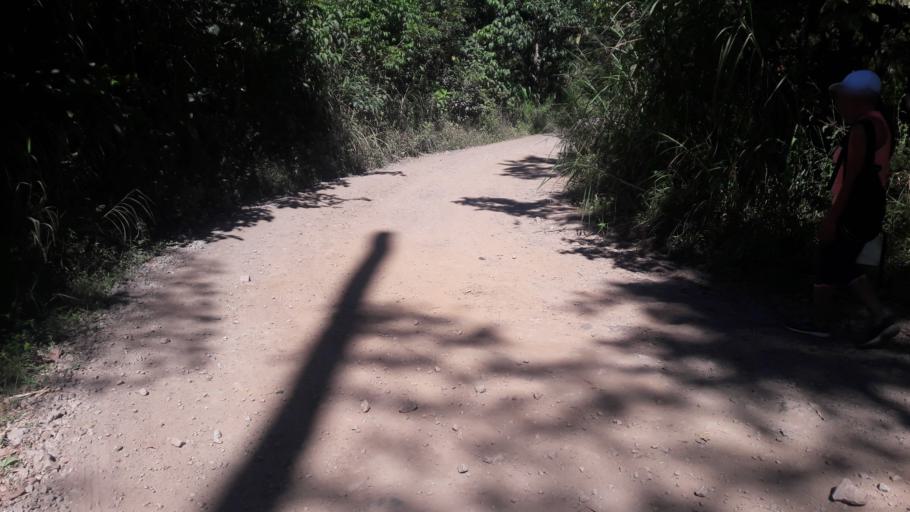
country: CO
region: Cundinamarca
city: Tenza
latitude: 5.0848
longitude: -73.4211
